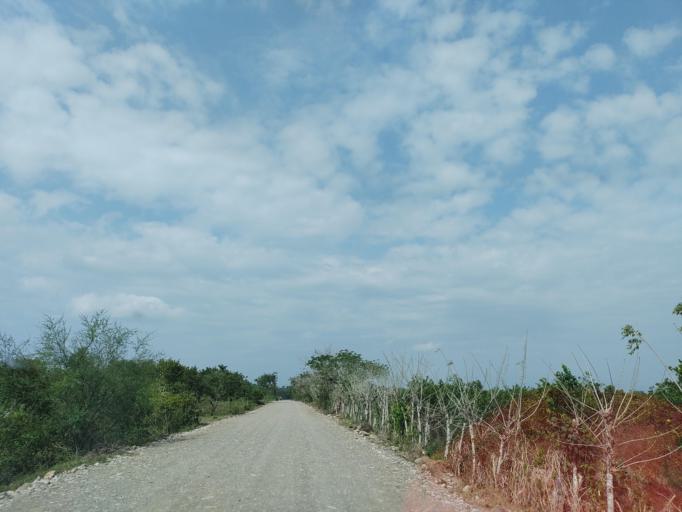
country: MX
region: Puebla
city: Espinal
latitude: 20.2818
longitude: -97.3351
